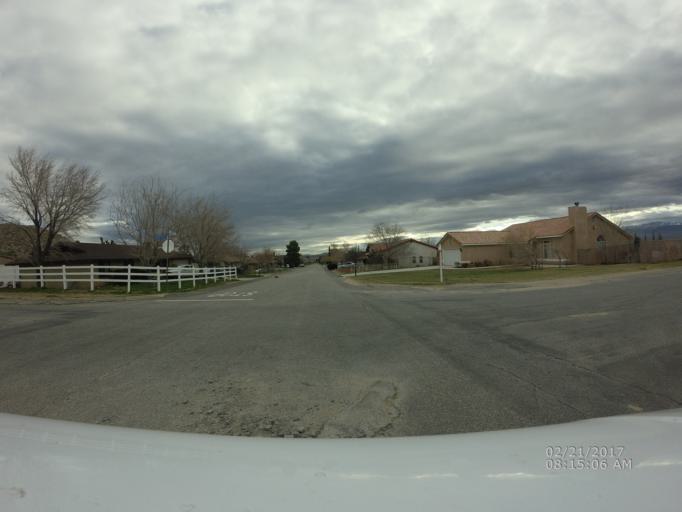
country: US
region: California
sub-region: Los Angeles County
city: Lake Los Angeles
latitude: 34.5968
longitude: -117.8395
